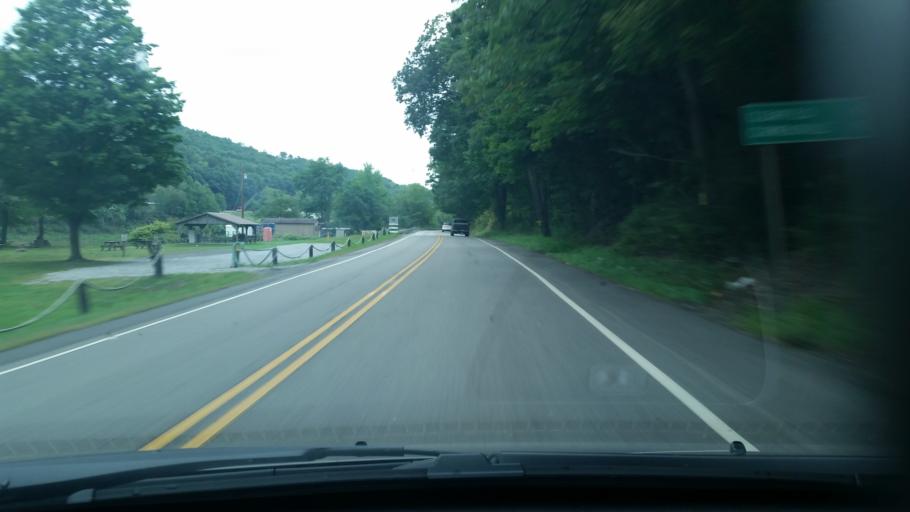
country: US
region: Pennsylvania
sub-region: Clearfield County
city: Clearfield
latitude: 41.0668
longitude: -78.3701
